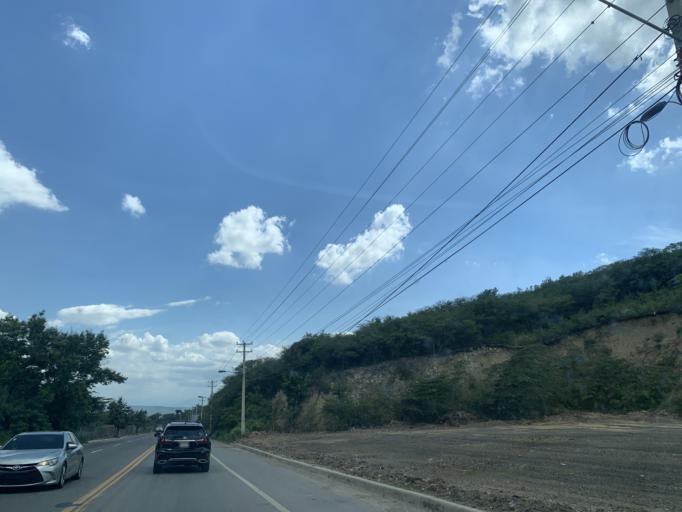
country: DO
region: Santiago
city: Villa Bisono
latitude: 19.5911
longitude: -70.8453
